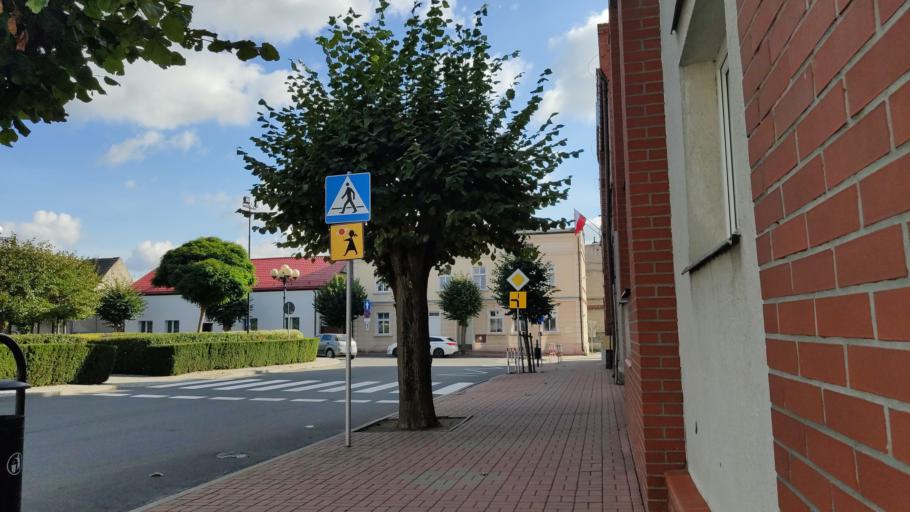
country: PL
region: Kujawsko-Pomorskie
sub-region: Powiat zninski
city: Barcin
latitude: 52.8642
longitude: 17.9443
